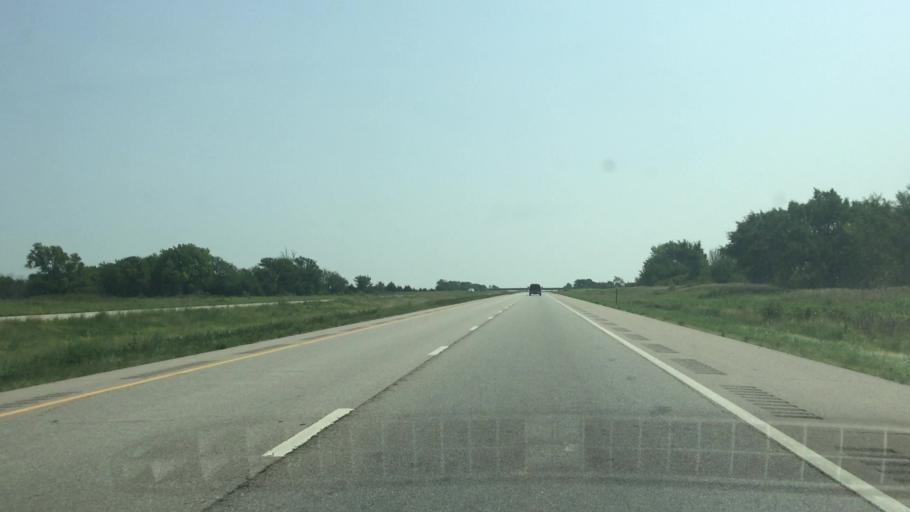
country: US
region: Kansas
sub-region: Lyon County
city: Emporia
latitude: 38.4102
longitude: -95.9623
